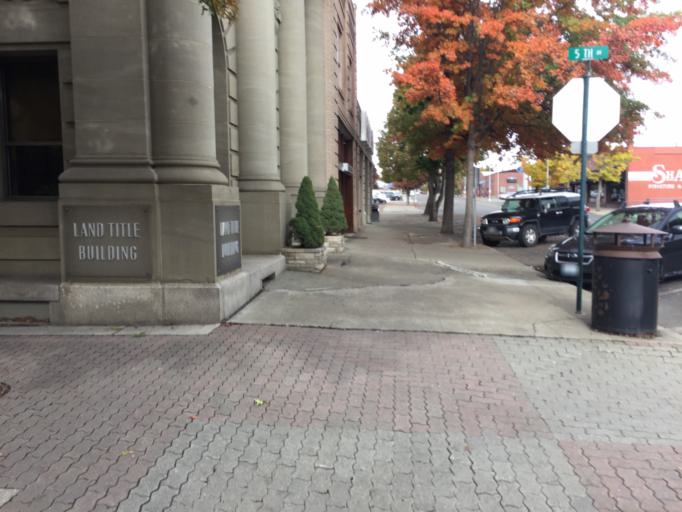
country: US
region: Washington
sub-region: Kittitas County
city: Ellensburg
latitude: 46.9966
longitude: -120.5475
